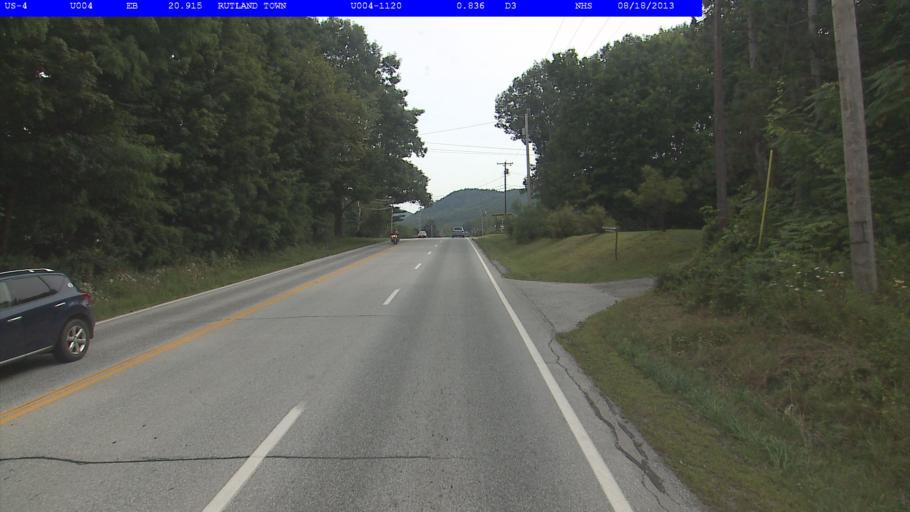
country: US
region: Vermont
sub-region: Rutland County
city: Rutland
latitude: 43.6309
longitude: -72.9431
